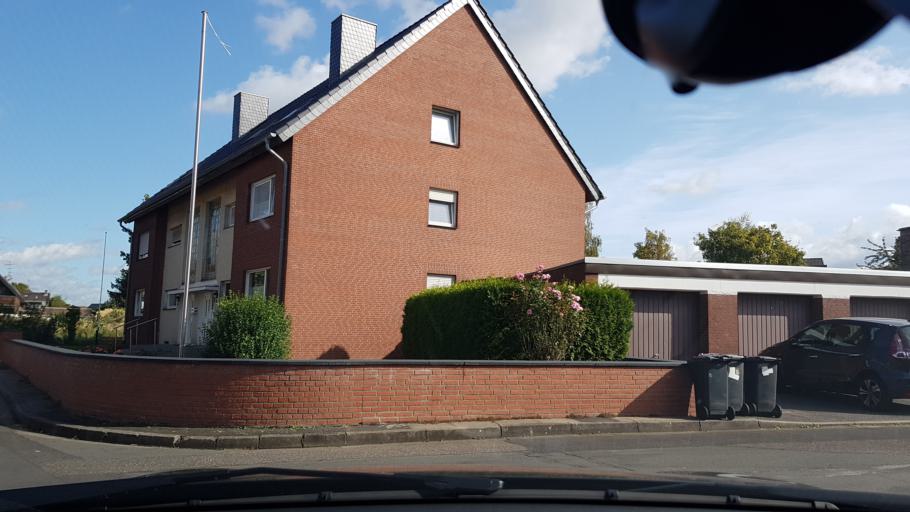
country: DE
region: North Rhine-Westphalia
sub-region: Regierungsbezirk Dusseldorf
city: Neuss
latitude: 51.1417
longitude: 6.7024
